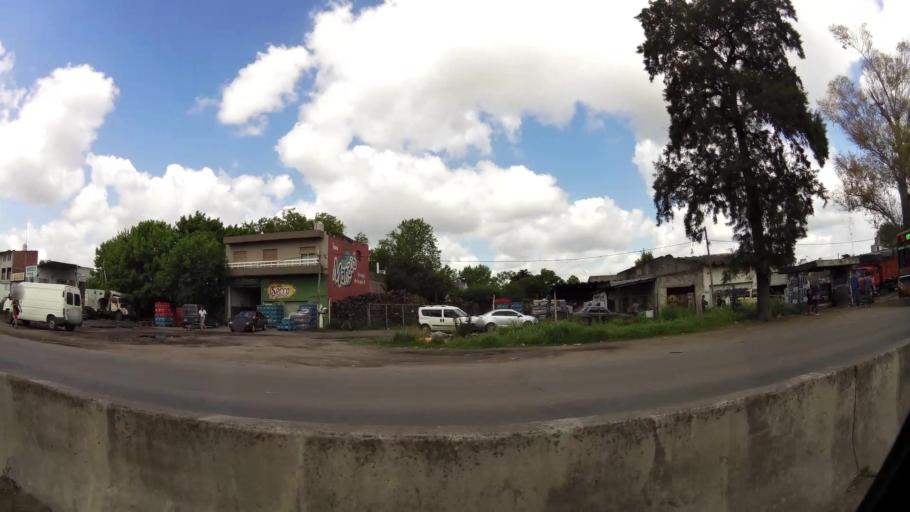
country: AR
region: Buenos Aires
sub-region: Partido de Quilmes
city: Quilmes
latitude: -34.8261
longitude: -58.2243
